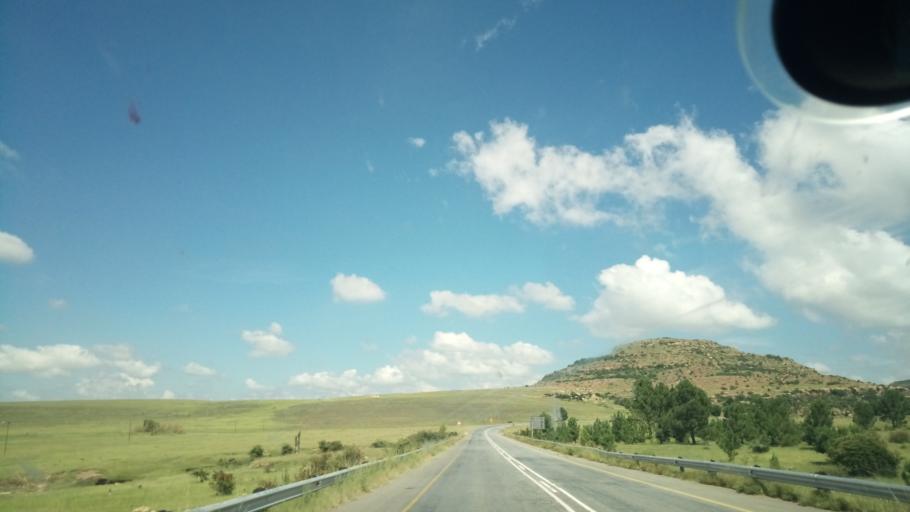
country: ZA
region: Orange Free State
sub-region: Thabo Mofutsanyana District Municipality
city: Ficksburg
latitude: -28.8924
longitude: 27.8514
